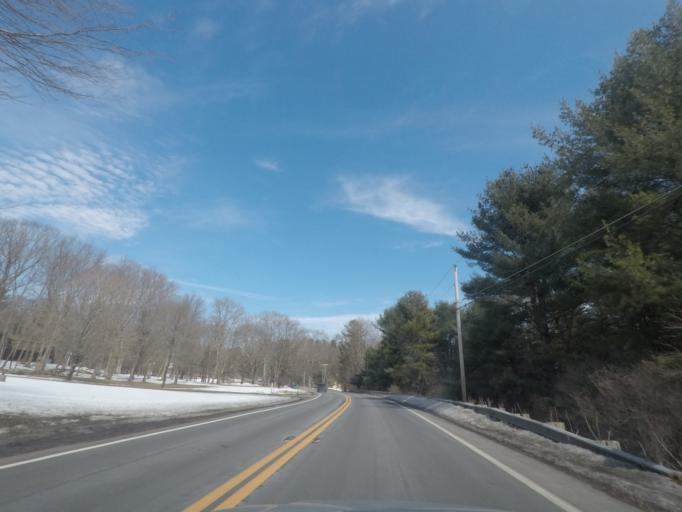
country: US
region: Massachusetts
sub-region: Berkshire County
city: West Stockbridge
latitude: 42.3534
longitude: -73.3832
